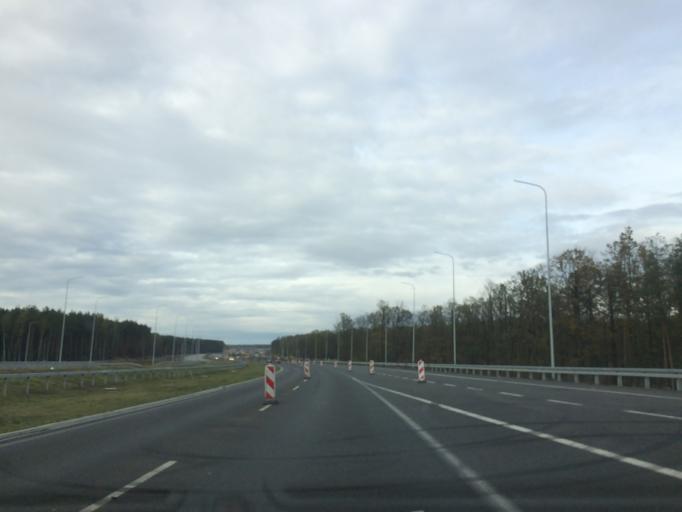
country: PL
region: Lower Silesian Voivodeship
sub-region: Powiat lubinski
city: Lubin
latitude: 51.4403
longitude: 16.1452
